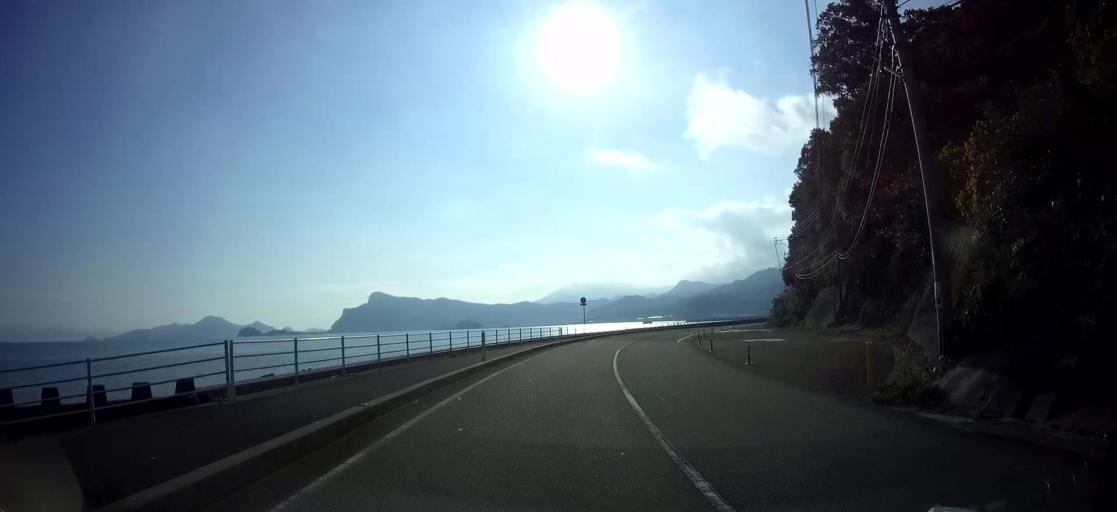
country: JP
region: Kumamoto
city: Yatsushiro
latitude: 32.4549
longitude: 130.4282
